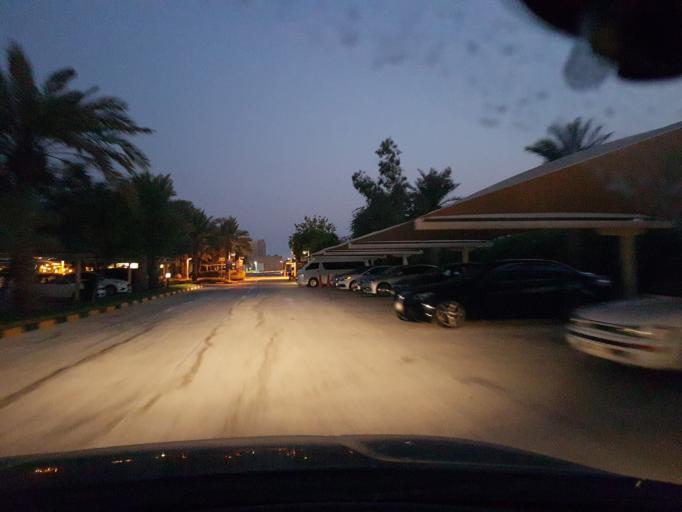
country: BH
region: Central Governorate
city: Dar Kulayb
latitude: 26.0153
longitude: 50.5086
